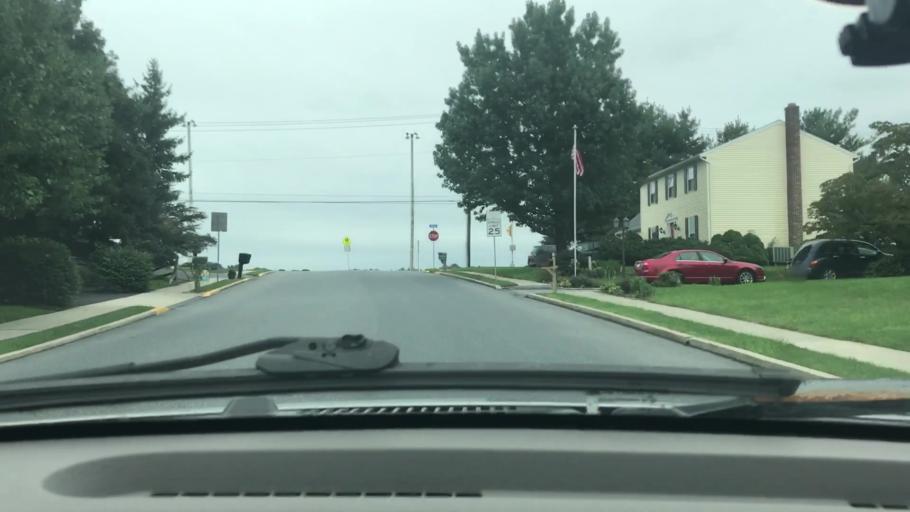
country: US
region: Pennsylvania
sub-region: Lancaster County
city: Elizabethtown
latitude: 40.1609
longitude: -76.5870
